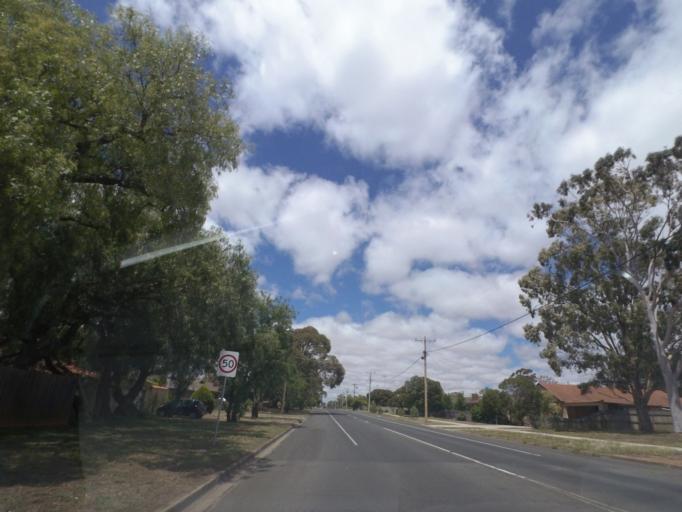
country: AU
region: Victoria
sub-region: Moorabool
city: Bacchus Marsh
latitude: -37.6546
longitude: 144.4431
